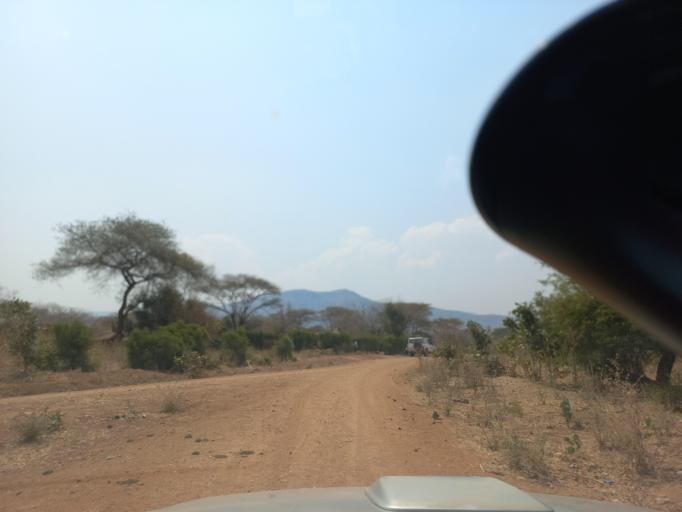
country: ZW
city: Chirundu
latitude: -15.9083
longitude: 28.6860
